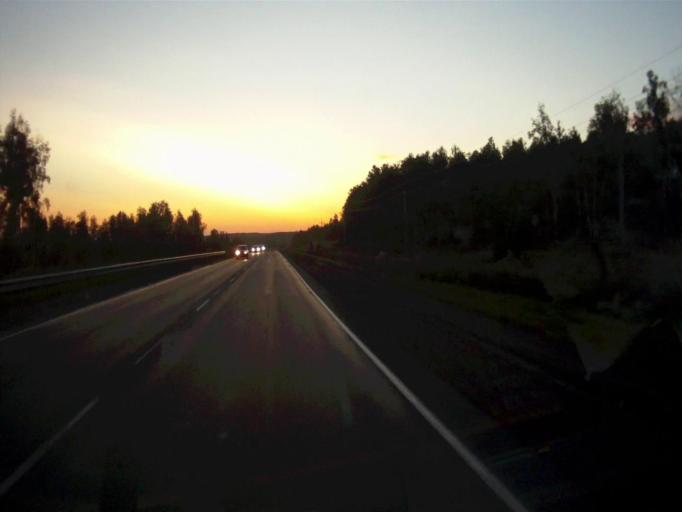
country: RU
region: Chelyabinsk
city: Poletayevo
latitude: 55.2219
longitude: 61.0163
